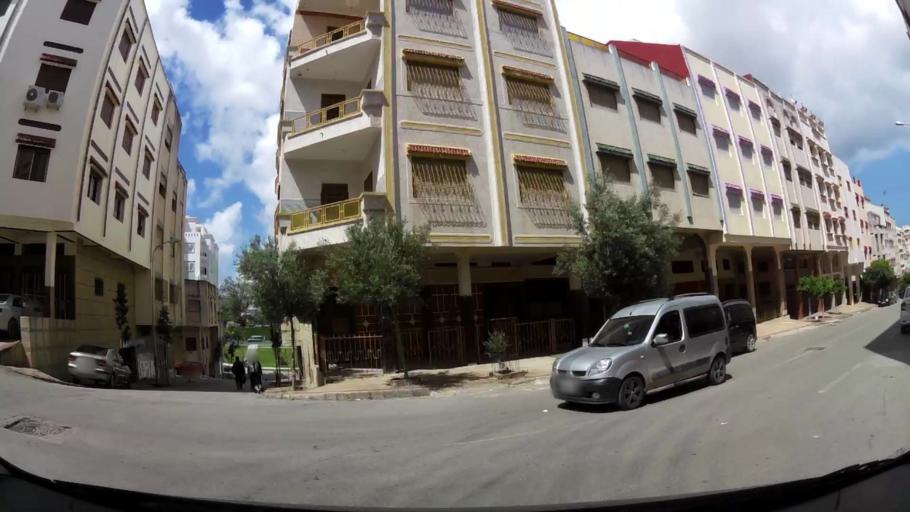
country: MA
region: Tanger-Tetouan
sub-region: Tanger-Assilah
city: Tangier
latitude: 35.7529
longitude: -5.8309
